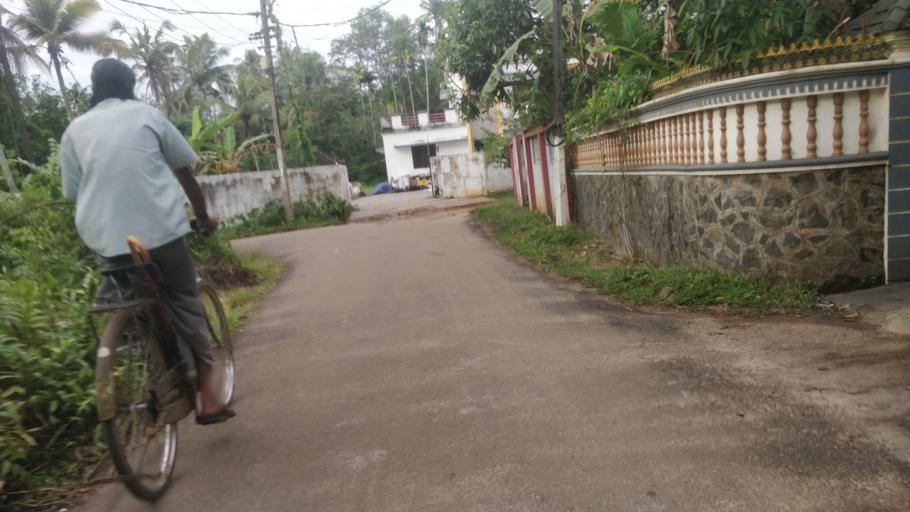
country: IN
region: Kerala
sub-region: Alappuzha
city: Shertallai
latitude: 9.6876
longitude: 76.3477
